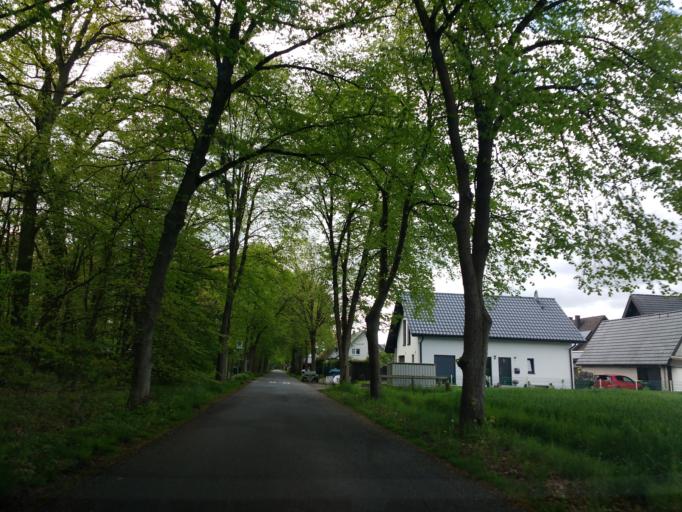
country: DE
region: North Rhine-Westphalia
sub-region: Regierungsbezirk Detmold
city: Hovelhof
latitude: 51.7958
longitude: 8.6819
